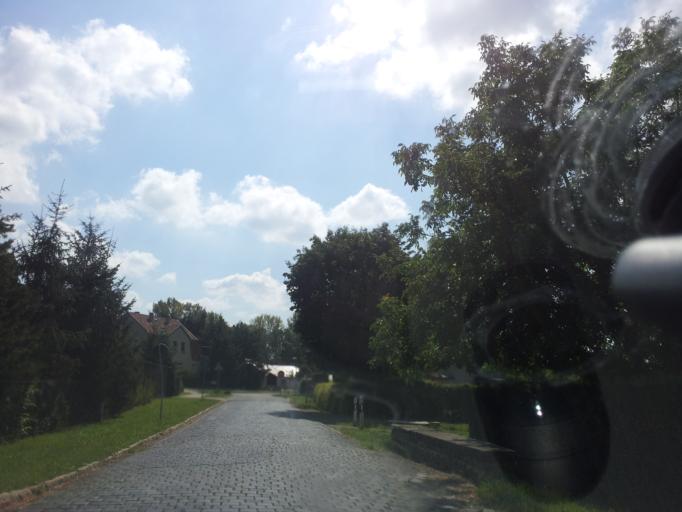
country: DE
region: Saxony-Anhalt
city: Weddersleben
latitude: 51.7613
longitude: 11.0887
